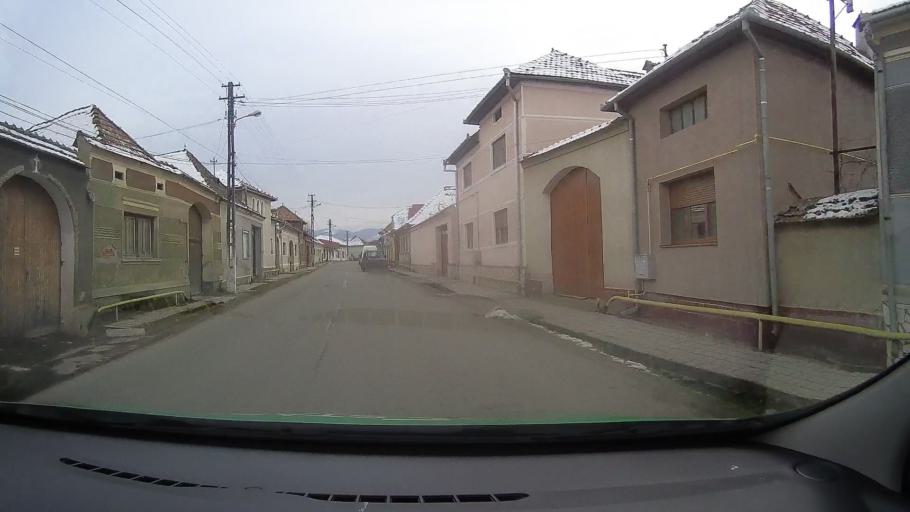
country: RO
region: Hunedoara
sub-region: Comuna Romos
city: Romos
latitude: 45.8432
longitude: 23.2740
